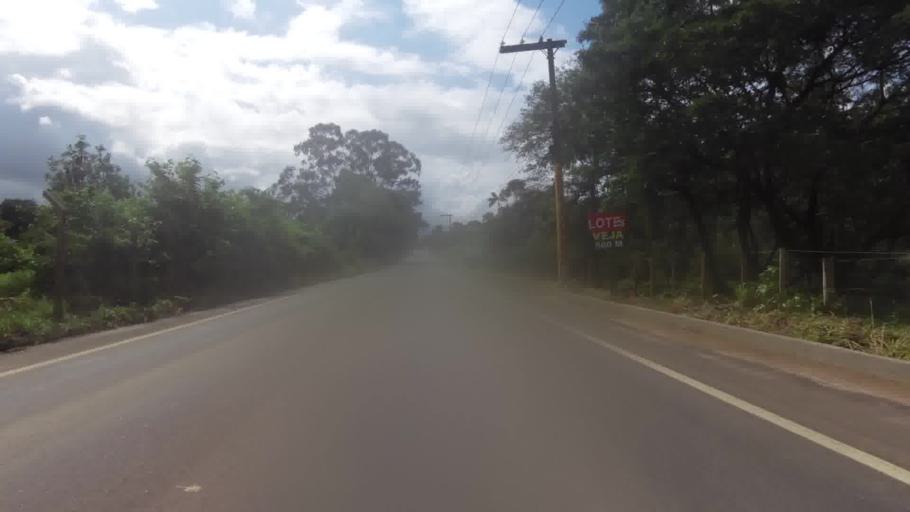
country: BR
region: Espirito Santo
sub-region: Piuma
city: Piuma
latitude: -20.8188
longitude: -40.6918
